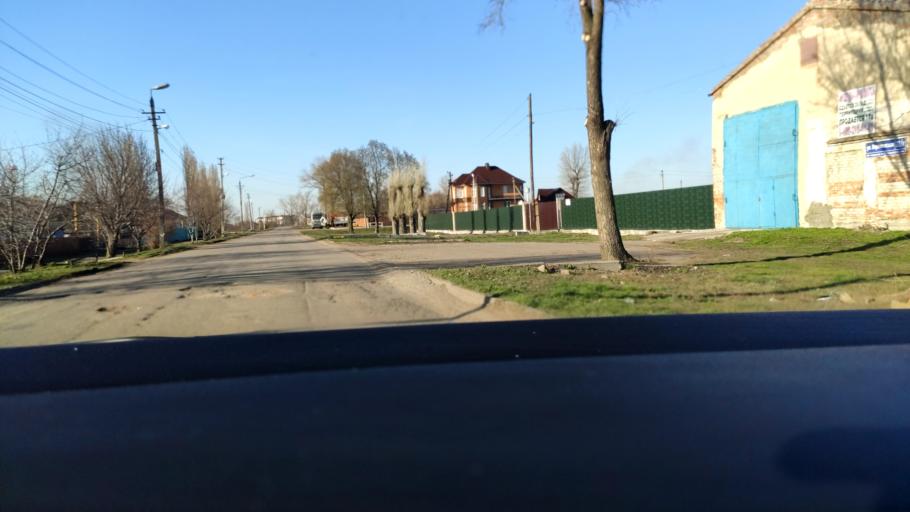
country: RU
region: Voronezj
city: Maslovka
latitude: 51.5070
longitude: 39.2939
